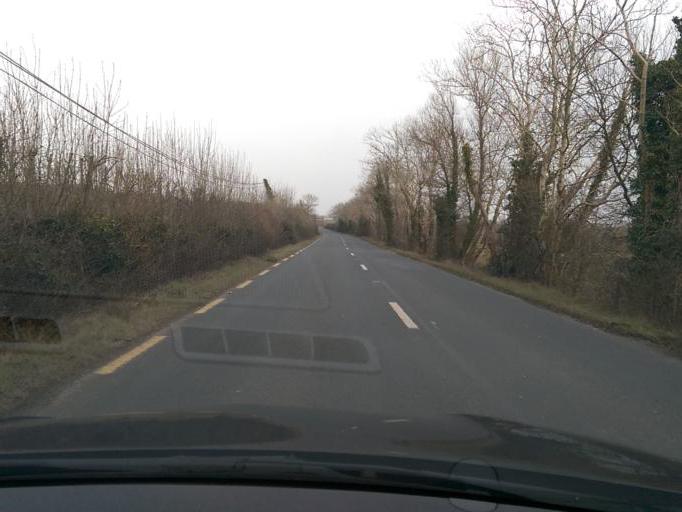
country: IE
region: Connaught
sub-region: Roscommon
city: Roscommon
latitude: 53.5100
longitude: -8.3656
